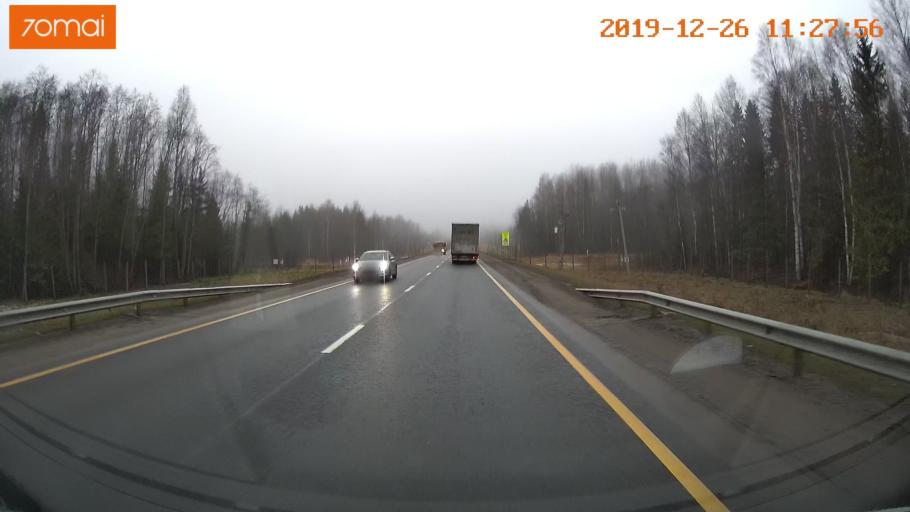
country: RU
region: Vologda
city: Chebsara
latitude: 59.1535
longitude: 38.8252
